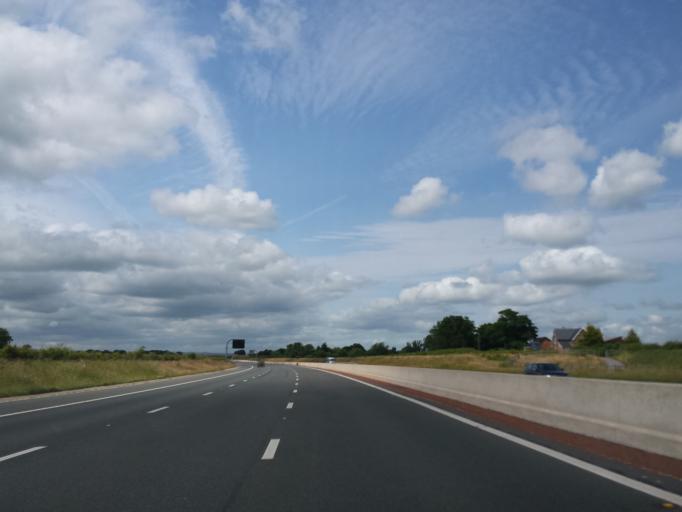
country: GB
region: England
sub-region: North Yorkshire
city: Bedale
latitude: 54.2773
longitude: -1.5313
